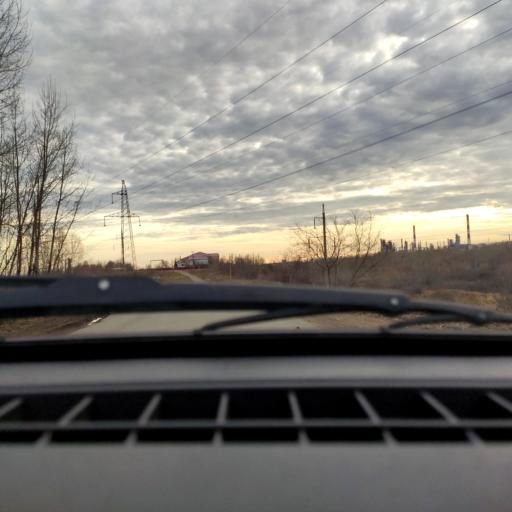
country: RU
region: Bashkortostan
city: Ufa
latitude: 54.8665
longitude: 56.1286
